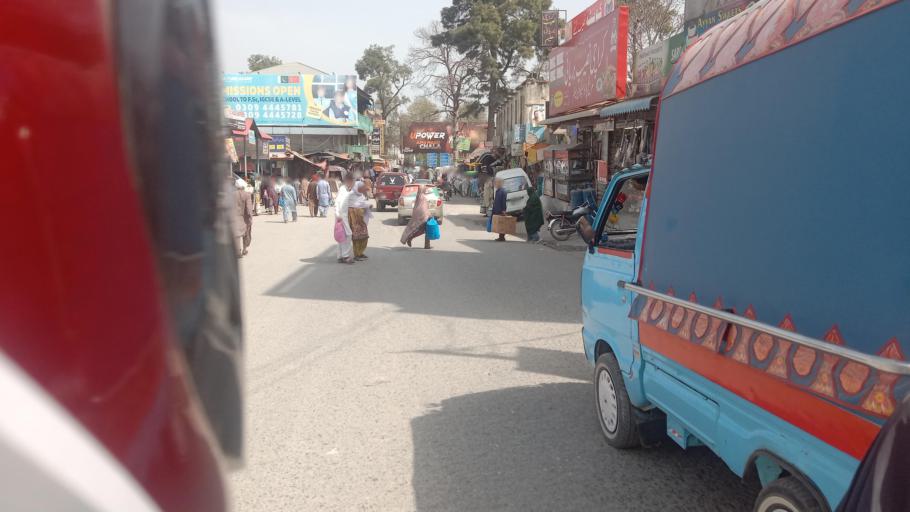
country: PK
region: Khyber Pakhtunkhwa
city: Abbottabad
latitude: 34.1406
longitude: 73.2128
